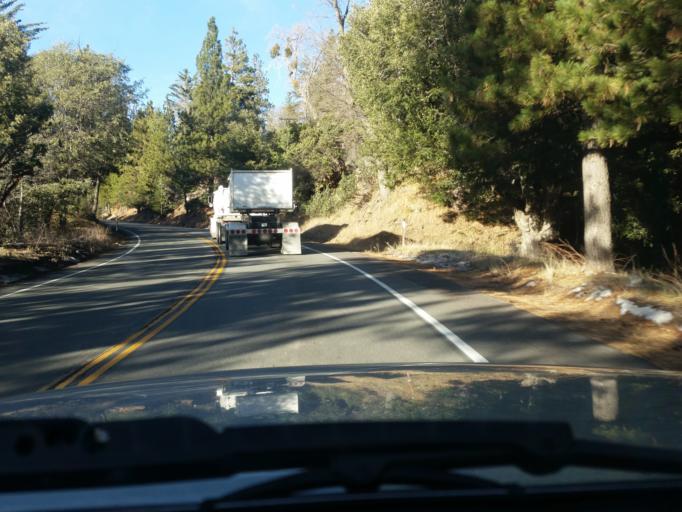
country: US
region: California
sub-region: San Bernardino County
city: Yucaipa
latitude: 34.1422
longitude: -116.9837
